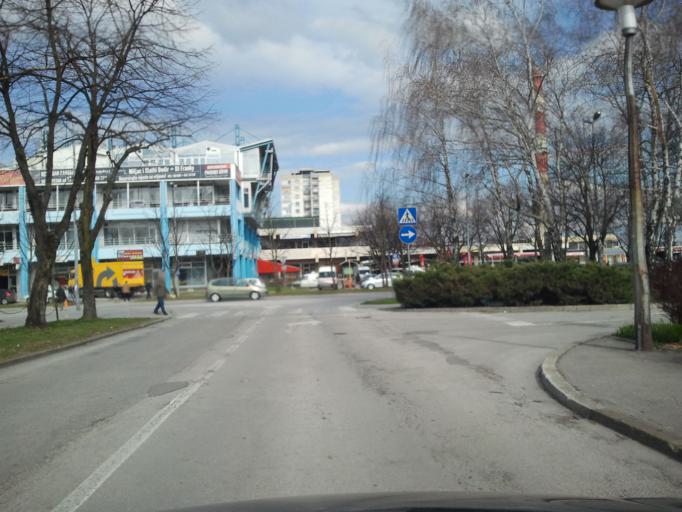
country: HR
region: Karlovacka
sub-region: Grad Karlovac
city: Karlovac
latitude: 45.4882
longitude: 15.5483
